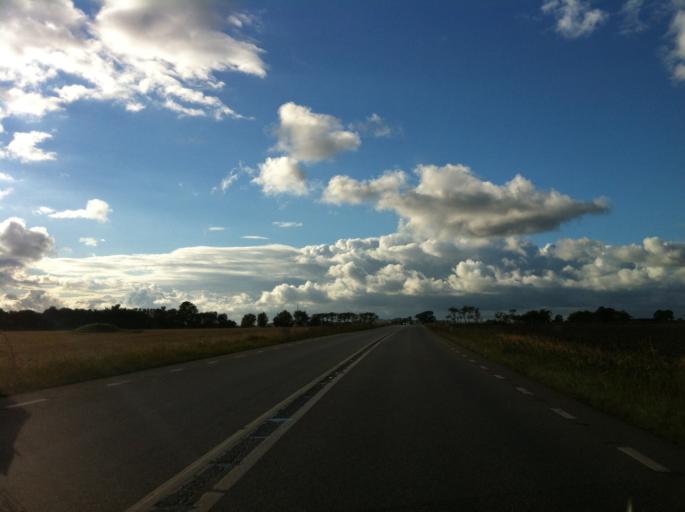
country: SE
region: Skane
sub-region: Svalovs Kommun
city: Teckomatorp
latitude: 55.8820
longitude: 13.0205
